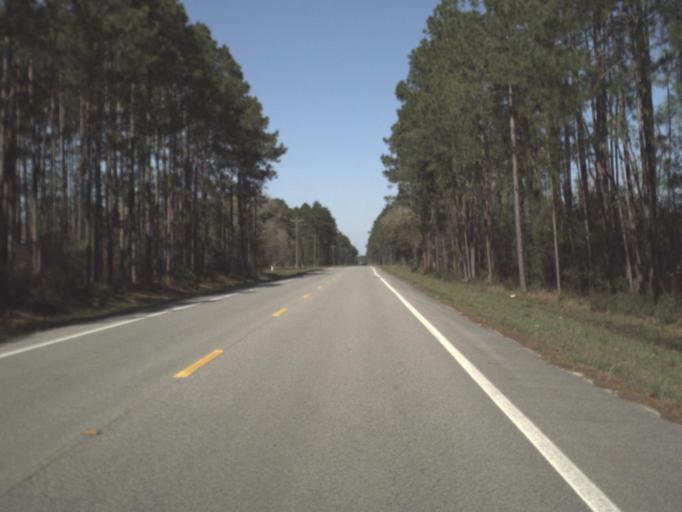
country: US
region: Florida
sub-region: Gulf County
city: Wewahitchka
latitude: 29.9537
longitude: -85.1798
